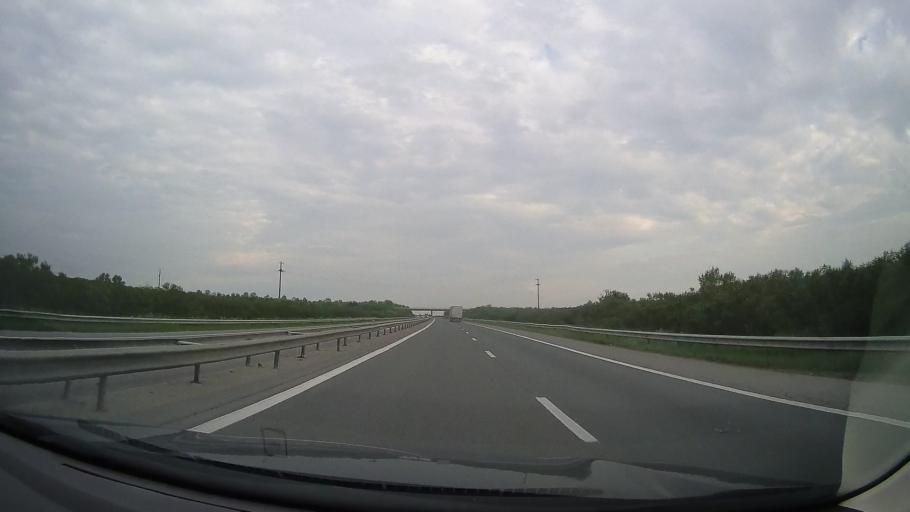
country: RO
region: Arges
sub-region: Comuna Ratesti
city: Ratesti
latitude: 44.7390
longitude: 25.1086
